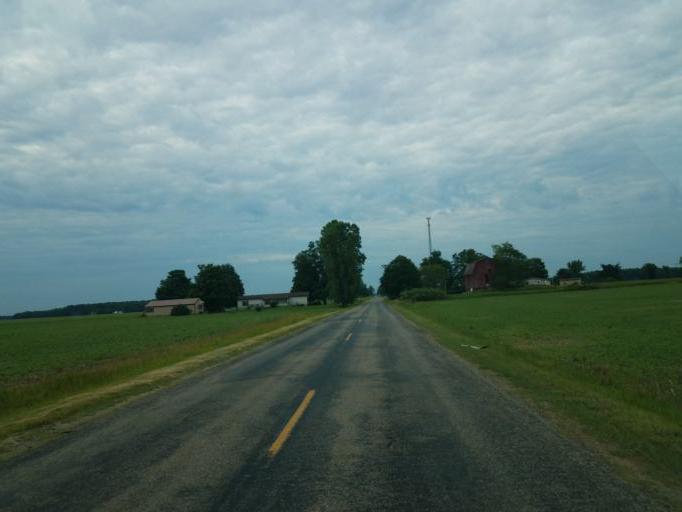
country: US
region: Michigan
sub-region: Barry County
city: Nashville
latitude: 42.6668
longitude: -84.9951
